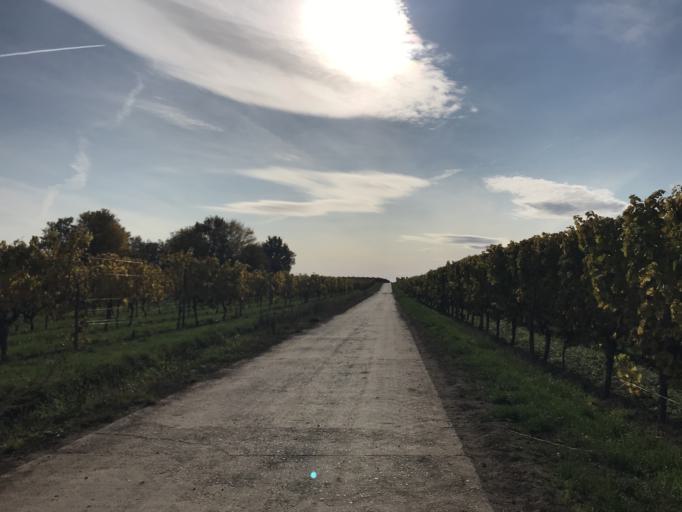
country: DE
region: Rheinland-Pfalz
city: Essenheim
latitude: 49.9254
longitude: 8.1493
